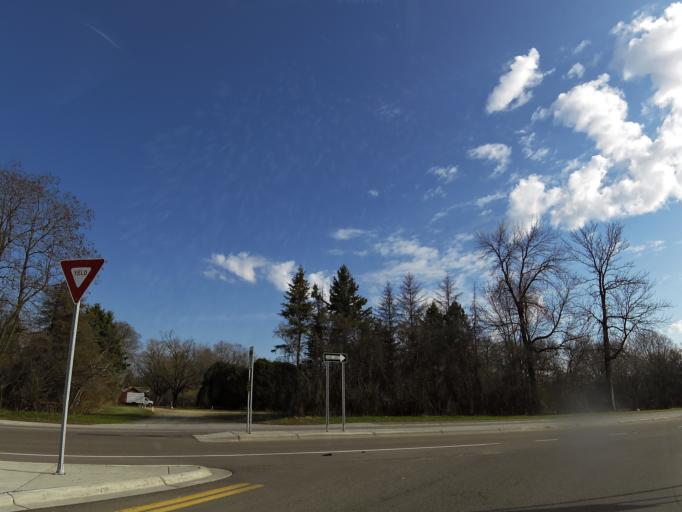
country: US
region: Minnesota
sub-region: Washington County
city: Cottage Grove
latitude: 44.8477
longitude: -92.9054
